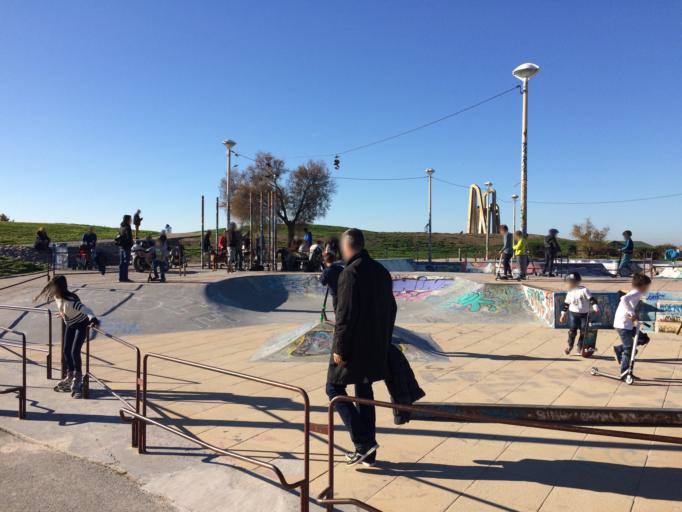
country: FR
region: Provence-Alpes-Cote d'Azur
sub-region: Departement des Bouches-du-Rhone
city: Marseille 08
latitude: 43.2519
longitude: 5.3749
